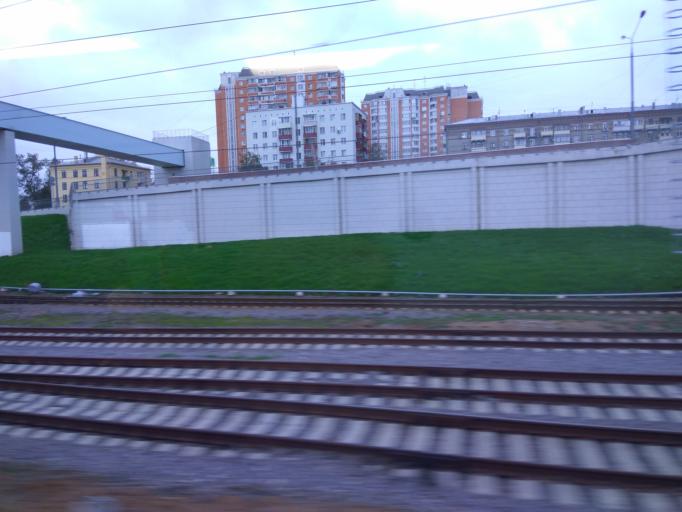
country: RU
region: Moskovskaya
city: Presnenskiy
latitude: 55.7594
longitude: 37.5236
